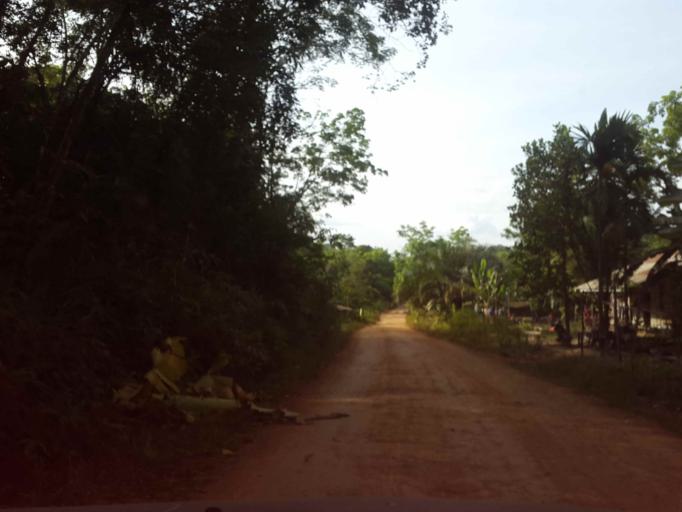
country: MY
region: Sarawak
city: Simanggang
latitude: 0.4391
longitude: 111.4689
